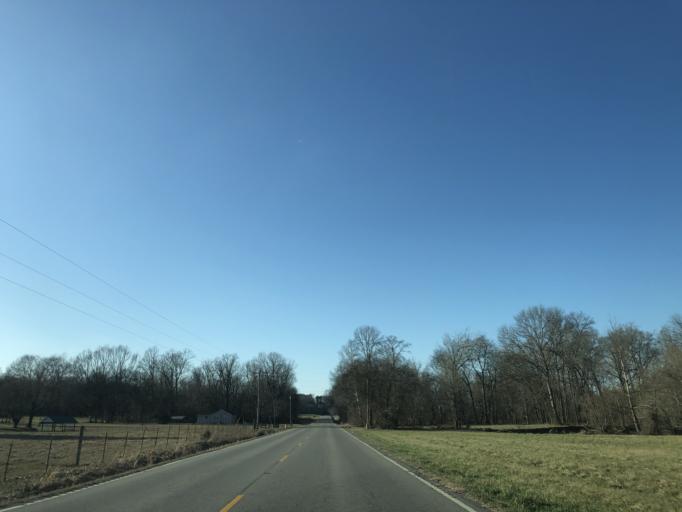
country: US
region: Tennessee
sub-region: Sumner County
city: White House
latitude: 36.5230
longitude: -86.6277
